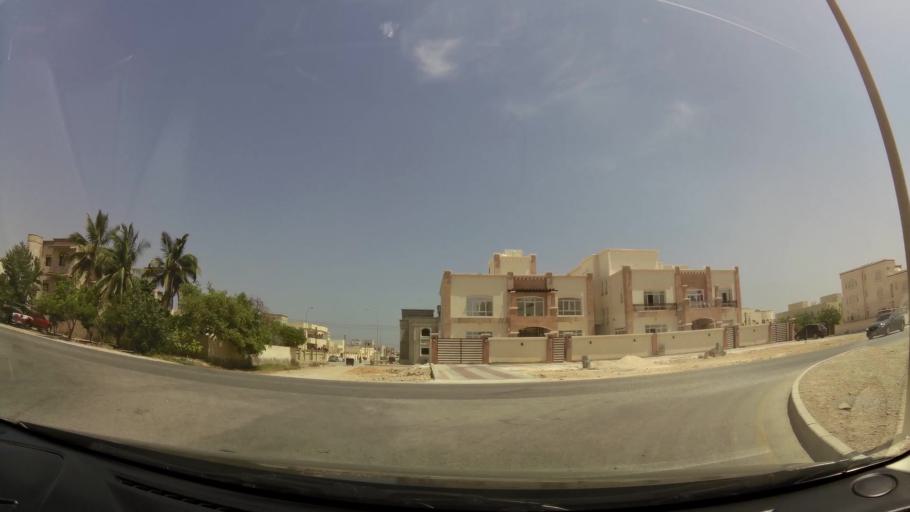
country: OM
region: Zufar
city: Salalah
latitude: 17.0503
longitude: 54.1570
